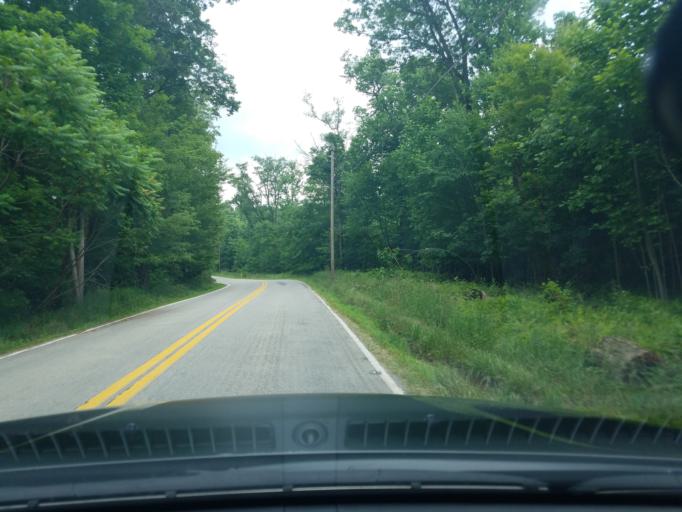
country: US
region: Pennsylvania
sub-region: Westmoreland County
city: Lawson Heights
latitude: 40.1904
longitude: -79.3846
